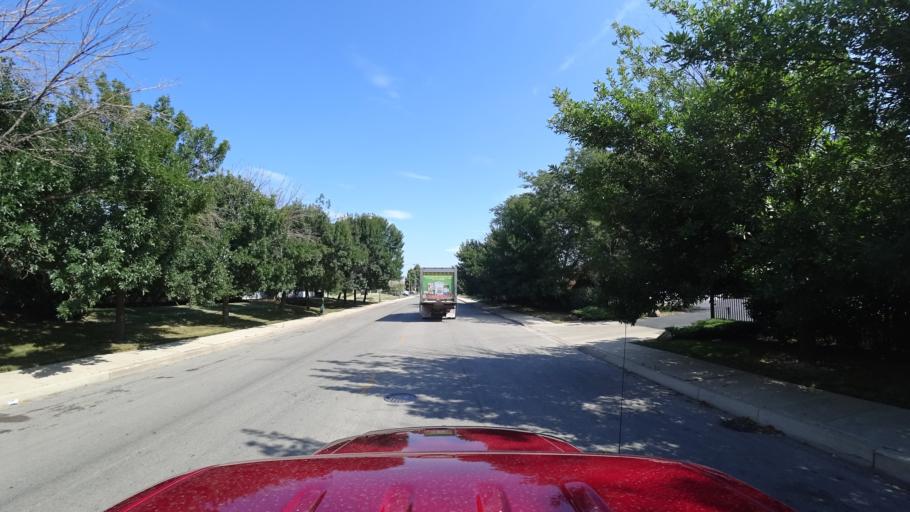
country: US
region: Illinois
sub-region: Cook County
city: Chicago
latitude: 41.8146
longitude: -87.6506
